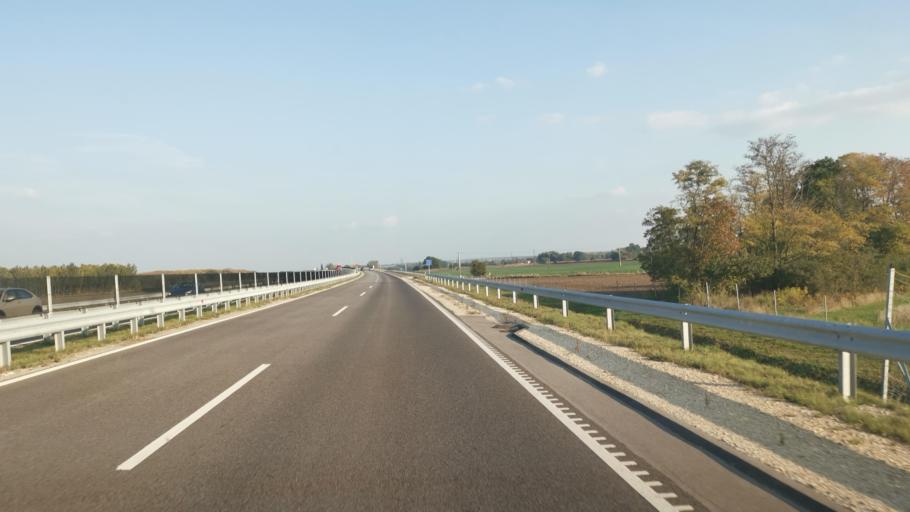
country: HU
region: Gyor-Moson-Sopron
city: Fertoszentmiklos
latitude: 47.5728
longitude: 16.7869
